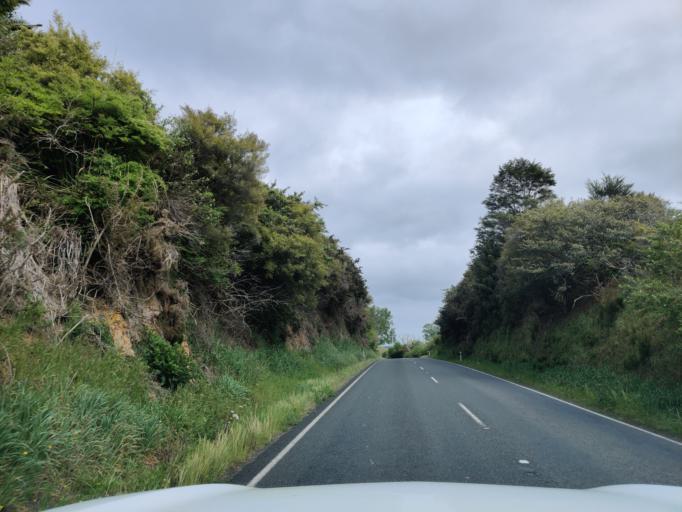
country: NZ
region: Waikato
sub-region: Waikato District
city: Ngaruawahia
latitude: -37.5769
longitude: 175.1289
